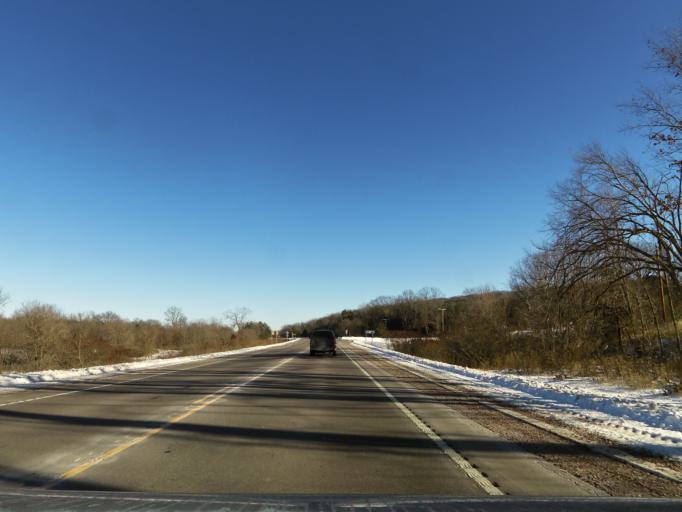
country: US
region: Wisconsin
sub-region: Columbia County
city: Portage
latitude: 43.5078
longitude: -89.5433
